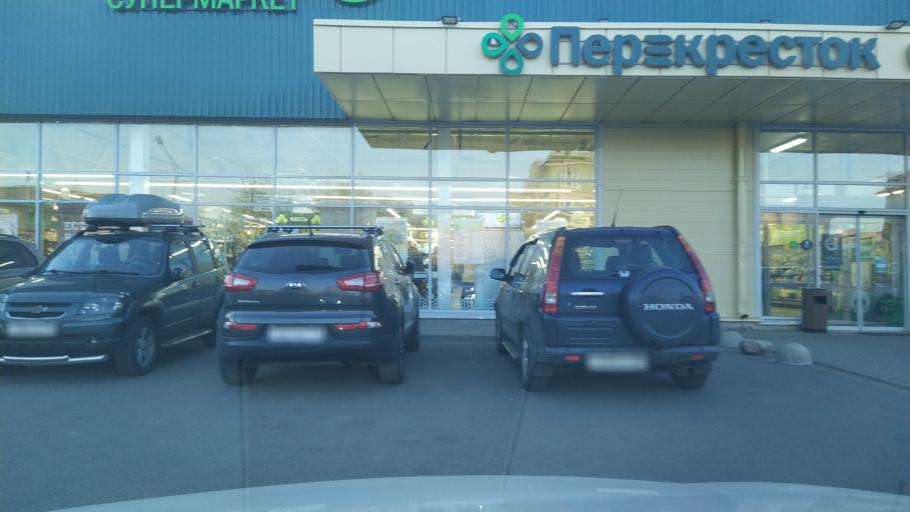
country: RU
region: St.-Petersburg
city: Pushkin
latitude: 59.7035
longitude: 30.3850
